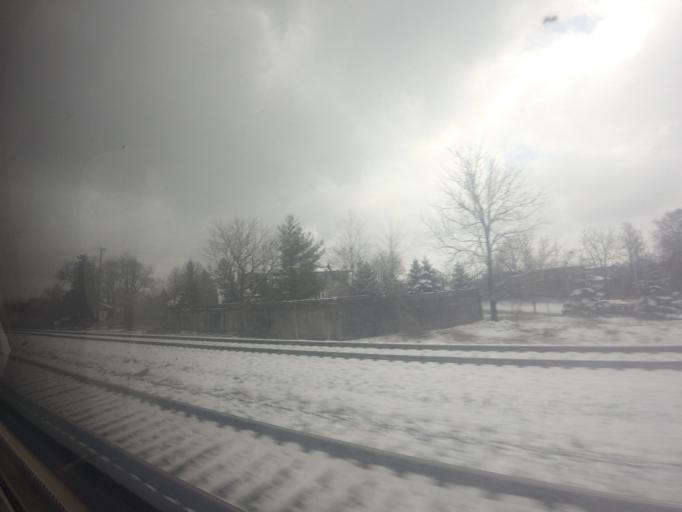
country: CA
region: Ontario
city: Scarborough
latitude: 43.6954
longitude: -79.2703
